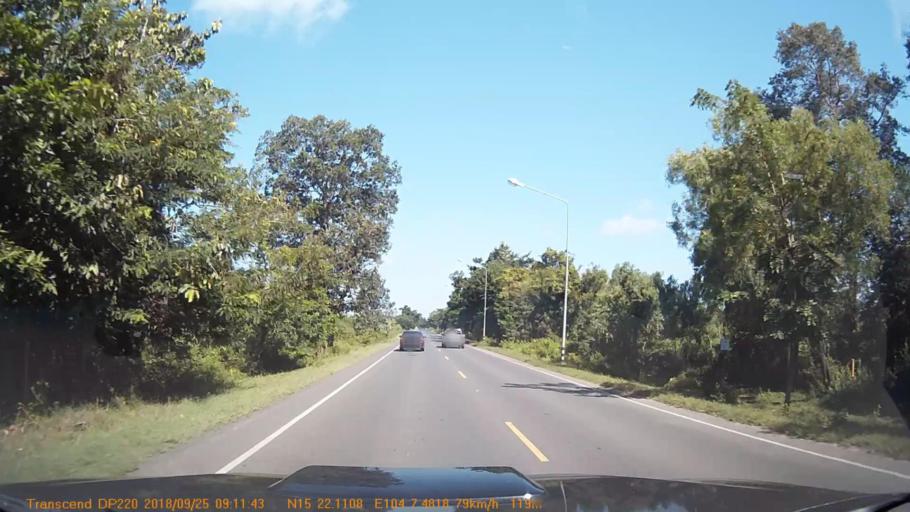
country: TH
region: Sisaket
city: Rasi Salai
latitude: 15.3685
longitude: 104.1247
